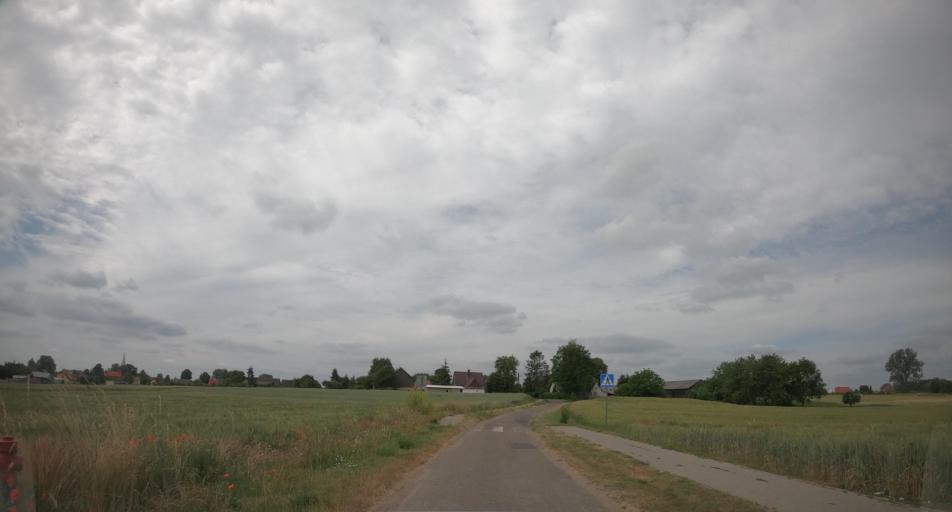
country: PL
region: West Pomeranian Voivodeship
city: Trzcinsko Zdroj
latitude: 52.9742
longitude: 14.6753
